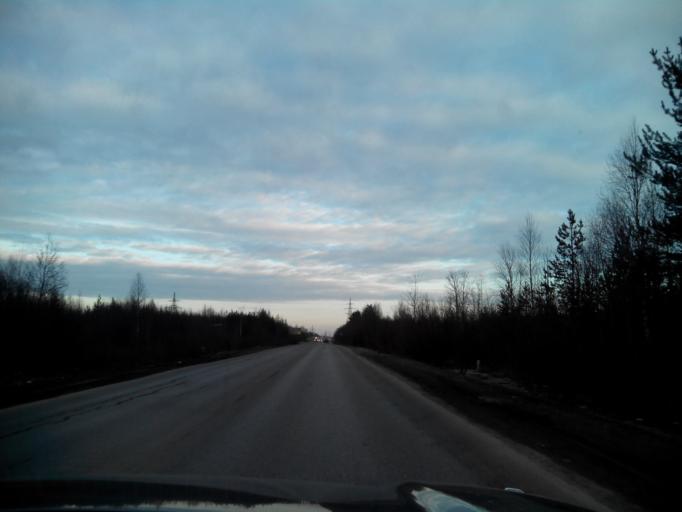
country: RU
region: Arkhangelskaya
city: Arkhangel'sk
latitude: 64.5229
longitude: 40.6688
